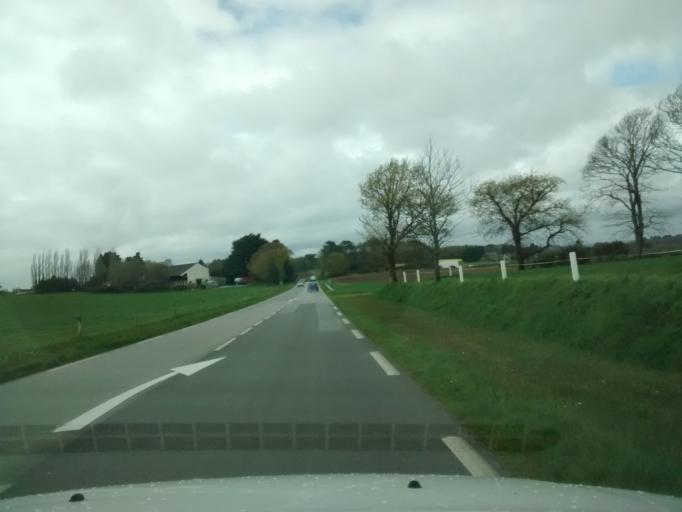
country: FR
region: Brittany
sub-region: Departement du Morbihan
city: Gestel
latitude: 47.7869
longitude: -3.4522
